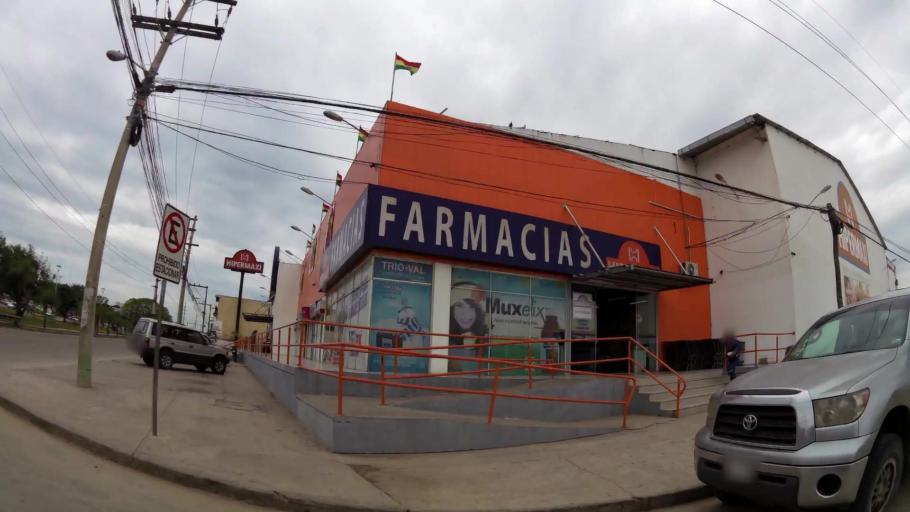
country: BO
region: Santa Cruz
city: Santa Cruz de la Sierra
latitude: -17.7499
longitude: -63.1851
